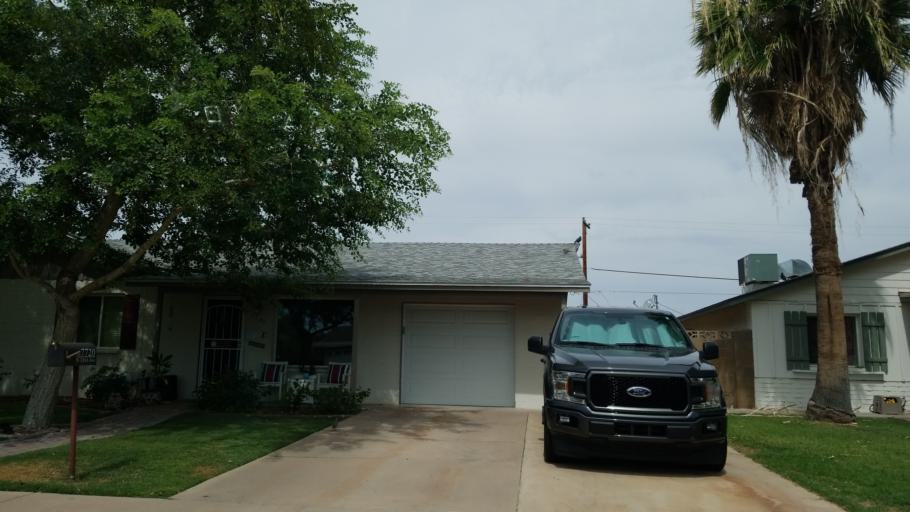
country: US
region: Arizona
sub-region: Maricopa County
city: Glendale
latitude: 33.5502
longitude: -112.0980
